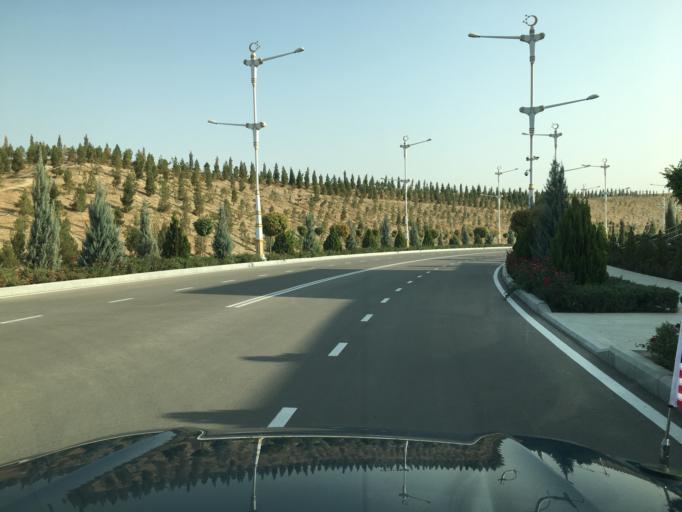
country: TM
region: Ahal
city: Ashgabat
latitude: 37.9382
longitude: 58.3122
